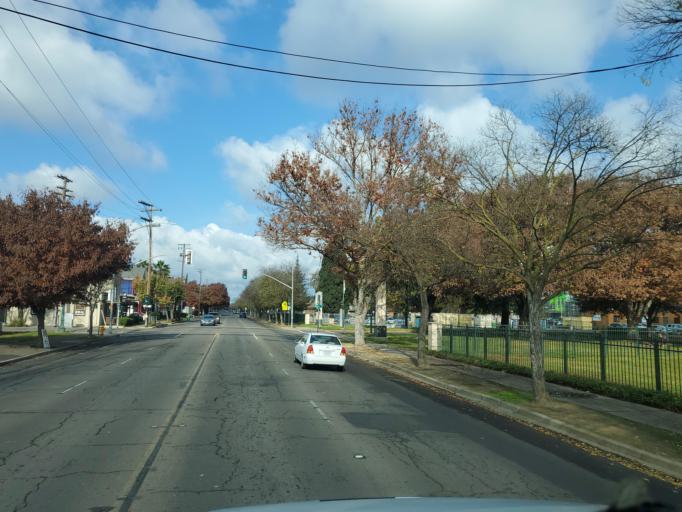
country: US
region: California
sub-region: San Joaquin County
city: Stockton
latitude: 37.9640
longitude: -121.2874
